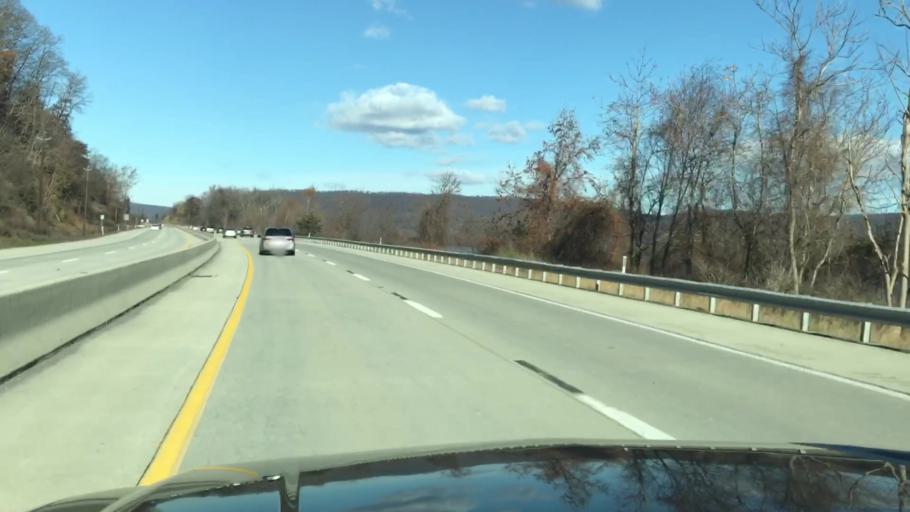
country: US
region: Pennsylvania
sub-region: Dauphin County
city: Matamoras
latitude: 40.4847
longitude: -76.9499
